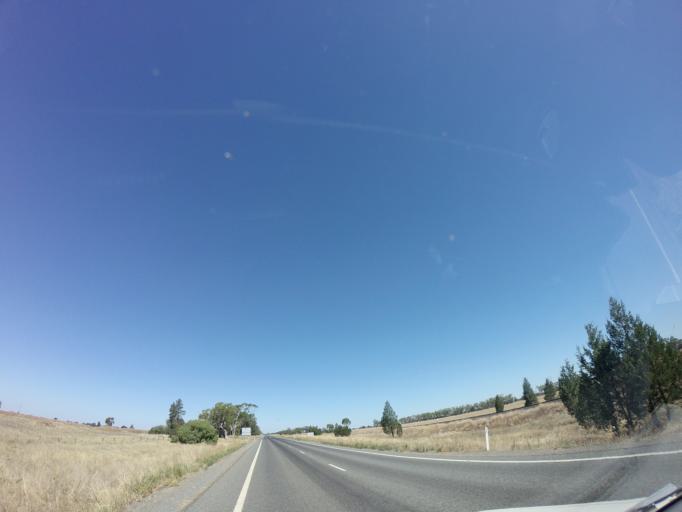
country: AU
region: New South Wales
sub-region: Bogan
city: Nyngan
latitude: -31.5813
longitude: 147.2329
